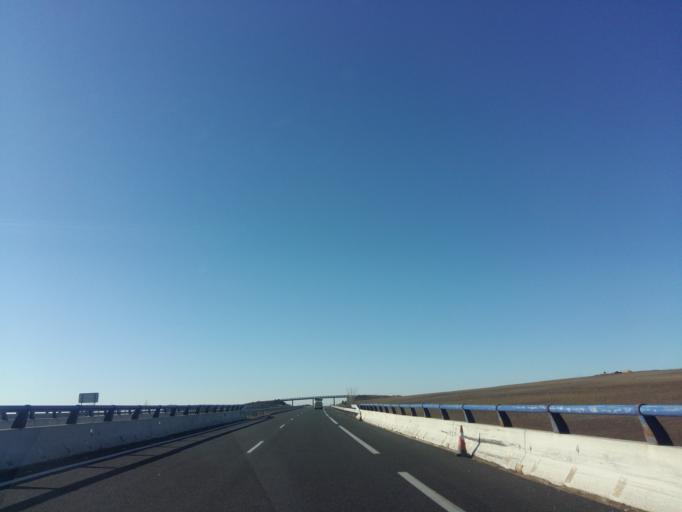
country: ES
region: Castille and Leon
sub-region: Provincia de Palencia
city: Espinosa de Villagonzalo
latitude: 42.4593
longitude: -4.3865
